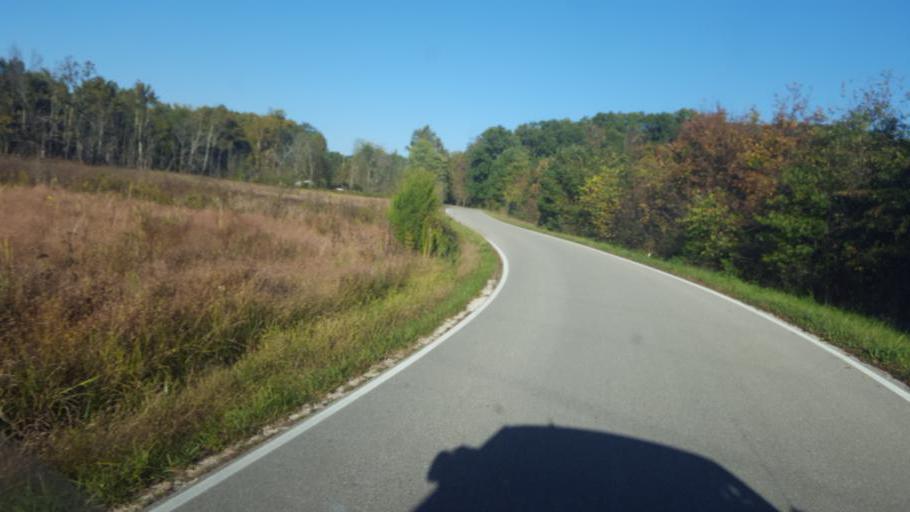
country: US
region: Ohio
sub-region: Adams County
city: Manchester
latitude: 38.5019
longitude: -83.5496
